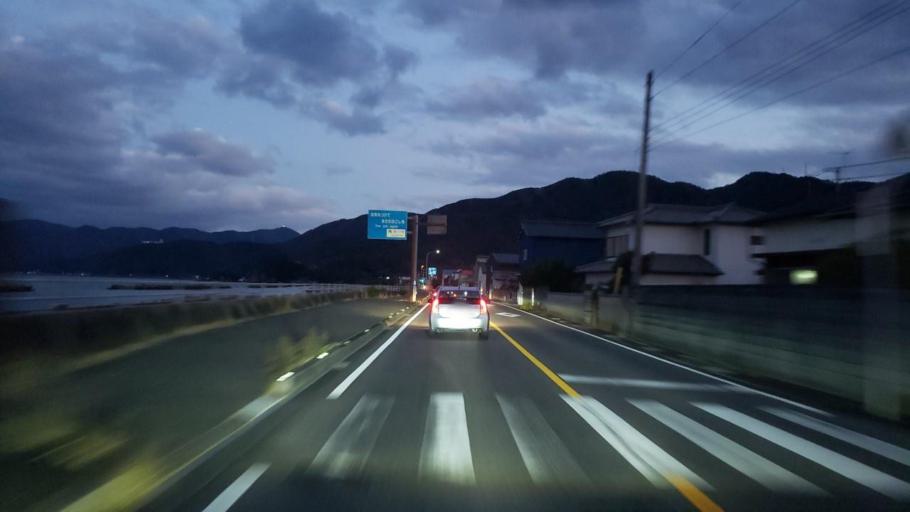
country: JP
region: Tokushima
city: Ishii
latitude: 34.2120
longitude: 134.4264
